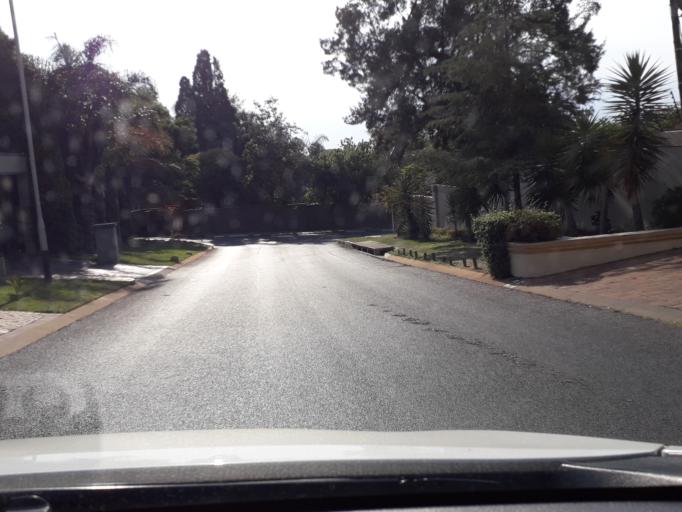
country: ZA
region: Gauteng
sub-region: City of Johannesburg Metropolitan Municipality
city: Roodepoort
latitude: -26.1550
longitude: 27.9590
